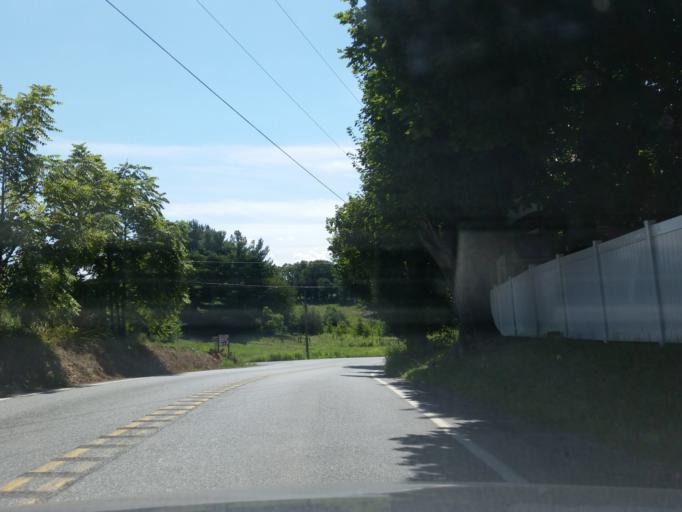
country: US
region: Pennsylvania
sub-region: Lebanon County
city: Palmyra
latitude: 40.3694
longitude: -76.6332
